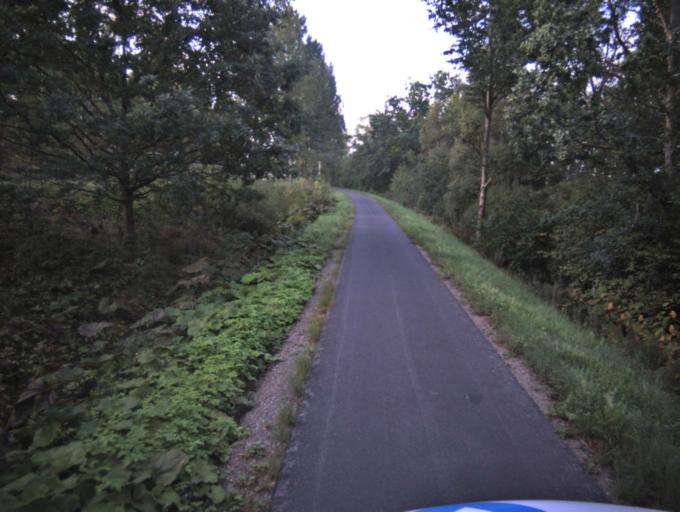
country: SE
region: Vaestra Goetaland
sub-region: Ulricehamns Kommun
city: Ulricehamn
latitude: 57.7476
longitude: 13.3930
